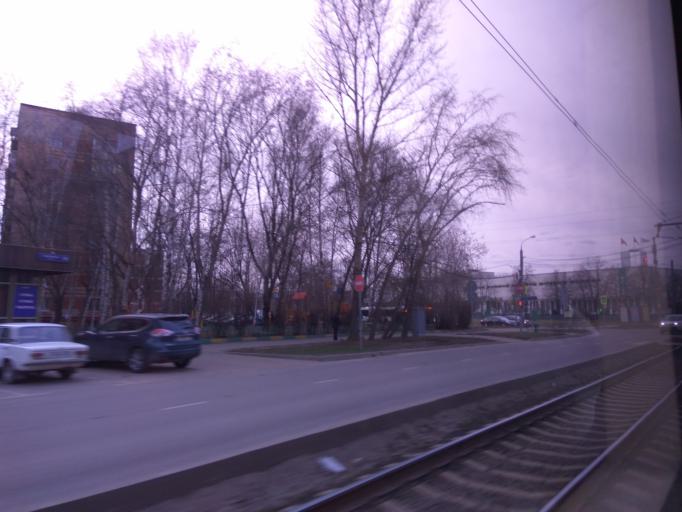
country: RU
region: Moscow
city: Kozeyevo
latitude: 55.8778
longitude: 37.6361
